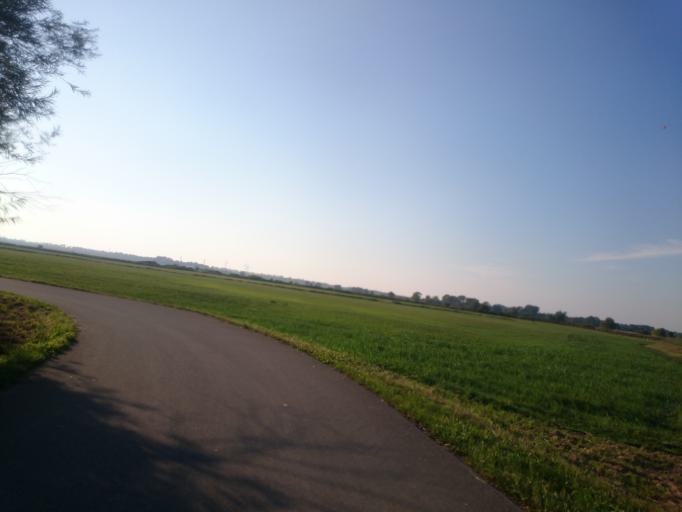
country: DE
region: Mecklenburg-Vorpommern
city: Velgast
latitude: 54.3478
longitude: 12.8068
